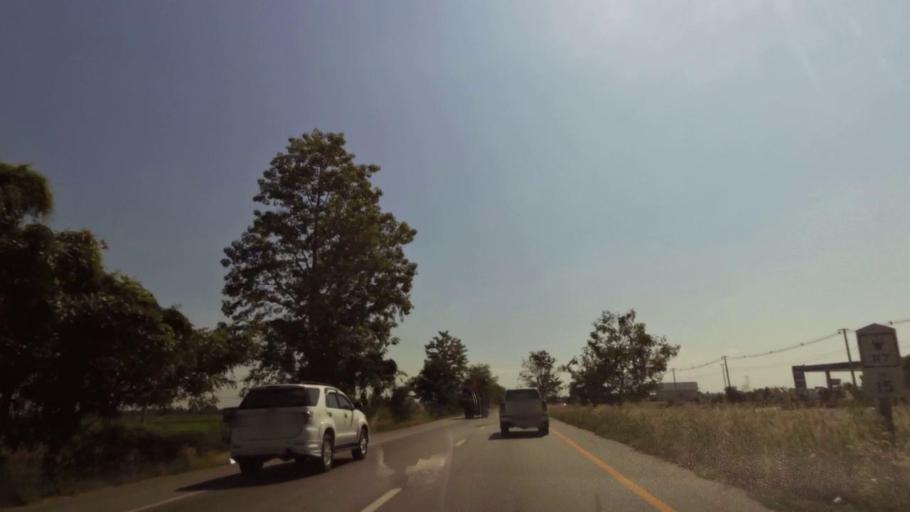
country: TH
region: Nakhon Sawan
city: Kao Liao
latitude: 15.8330
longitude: 100.1181
